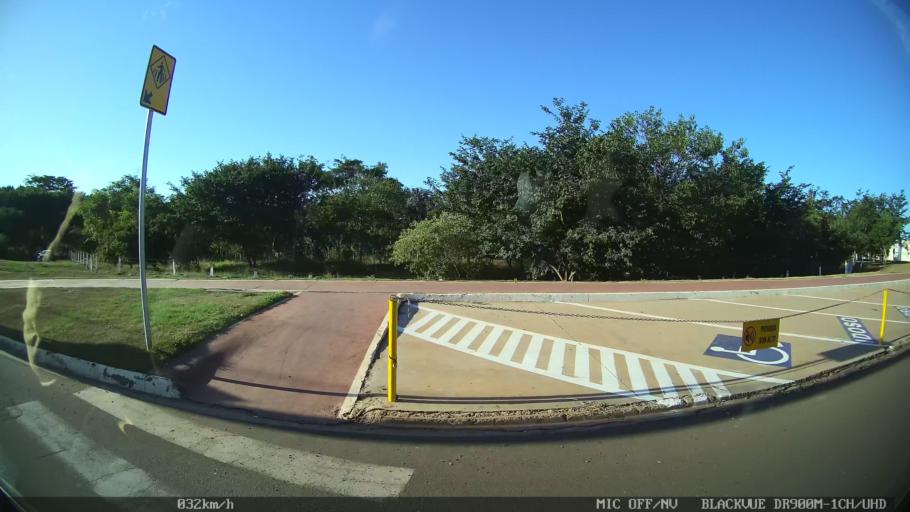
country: BR
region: Sao Paulo
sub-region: Guapiacu
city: Guapiacu
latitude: -20.7947
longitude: -49.2300
